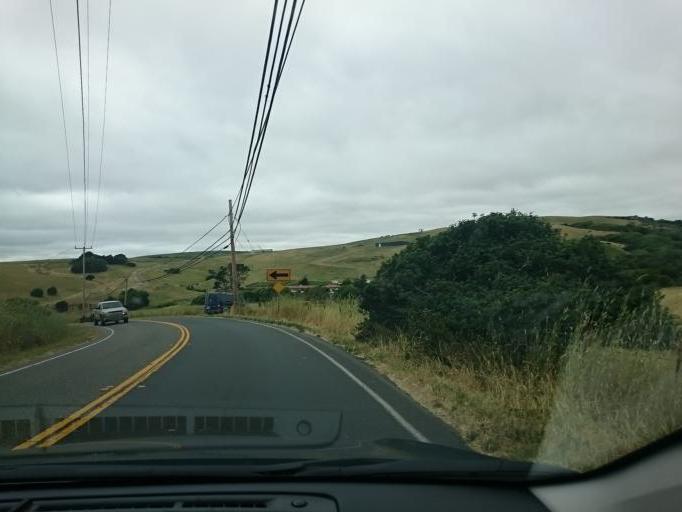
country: US
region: California
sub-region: Marin County
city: Inverness
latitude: 38.0915
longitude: -122.8143
